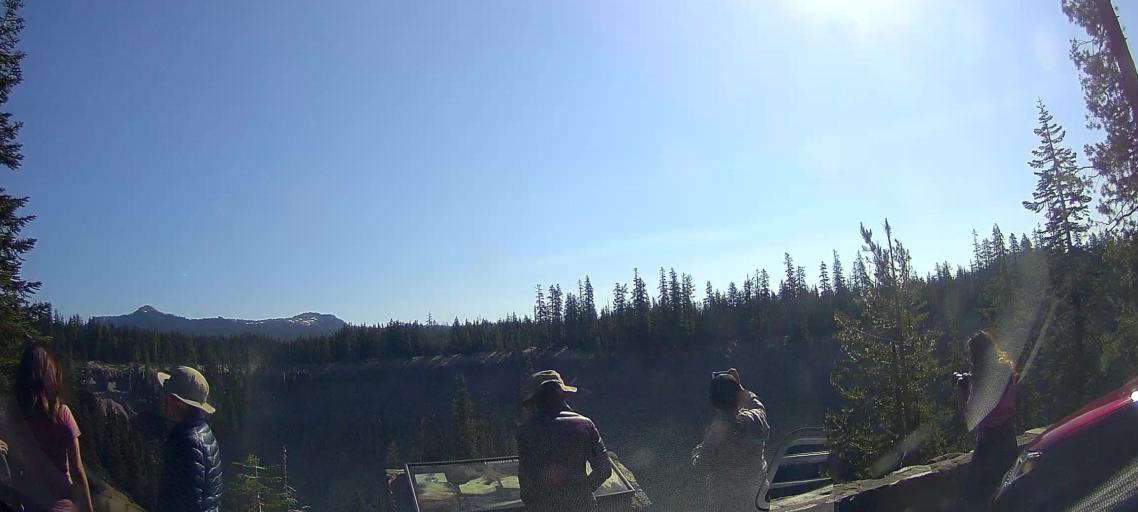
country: US
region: Oregon
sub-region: Jackson County
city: Shady Cove
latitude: 42.8580
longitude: -122.1539
